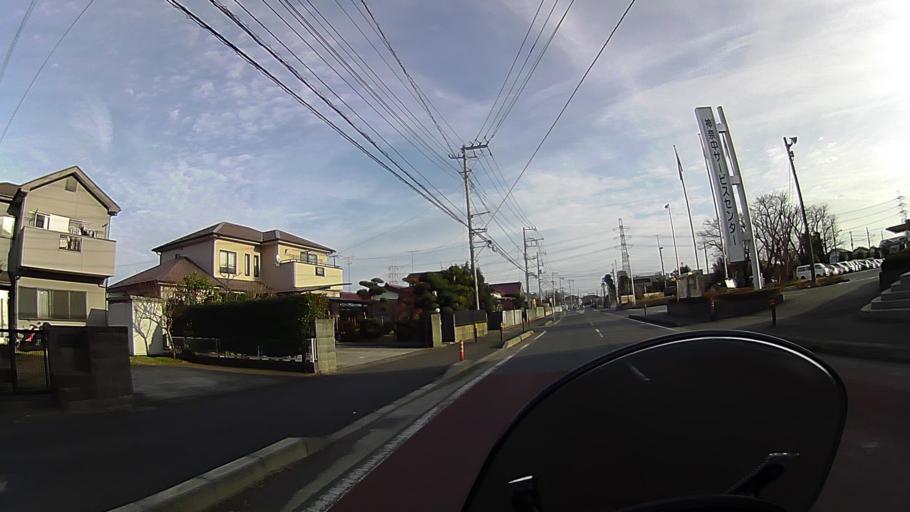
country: JP
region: Kanagawa
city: Minami-rinkan
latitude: 35.4263
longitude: 139.4278
